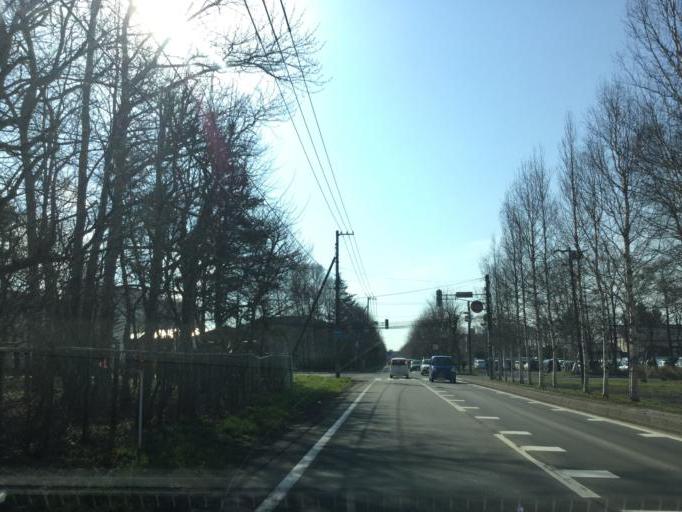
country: JP
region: Hokkaido
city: Ebetsu
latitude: 43.1175
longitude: 141.5485
